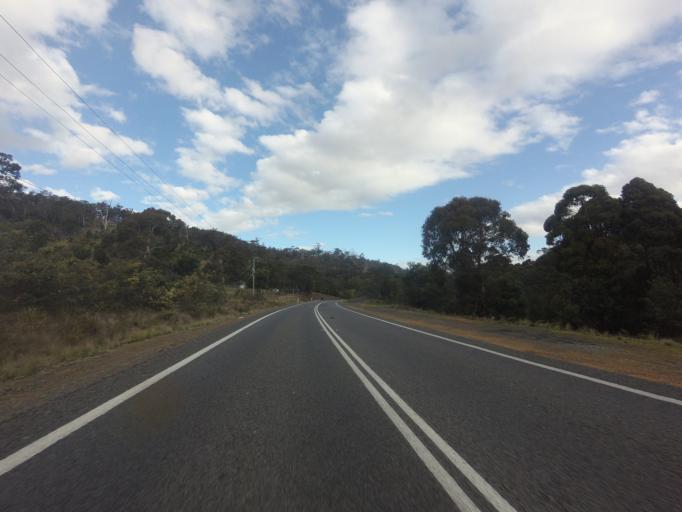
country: AU
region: Tasmania
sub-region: Sorell
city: Sorell
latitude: -42.6799
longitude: 147.5297
